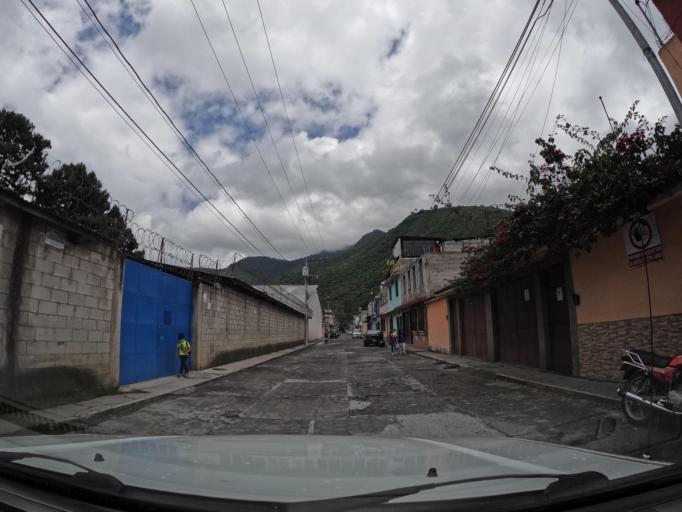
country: GT
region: Sacatepequez
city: Jocotenango
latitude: 14.5785
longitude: -90.7465
